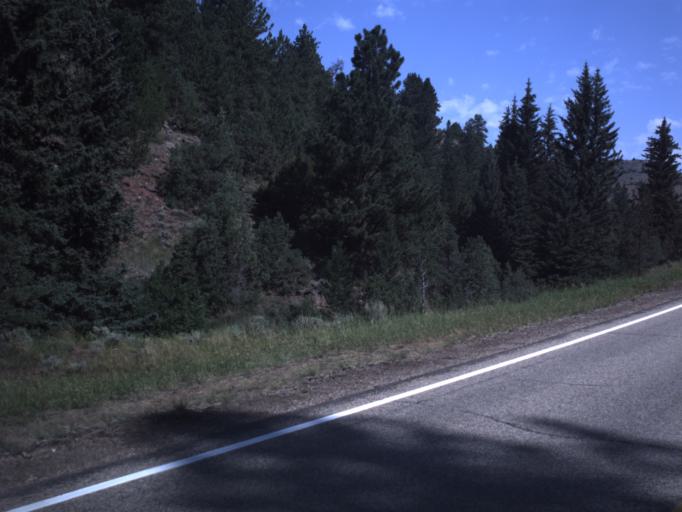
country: US
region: Utah
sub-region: Daggett County
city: Manila
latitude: 40.8755
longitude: -109.6919
